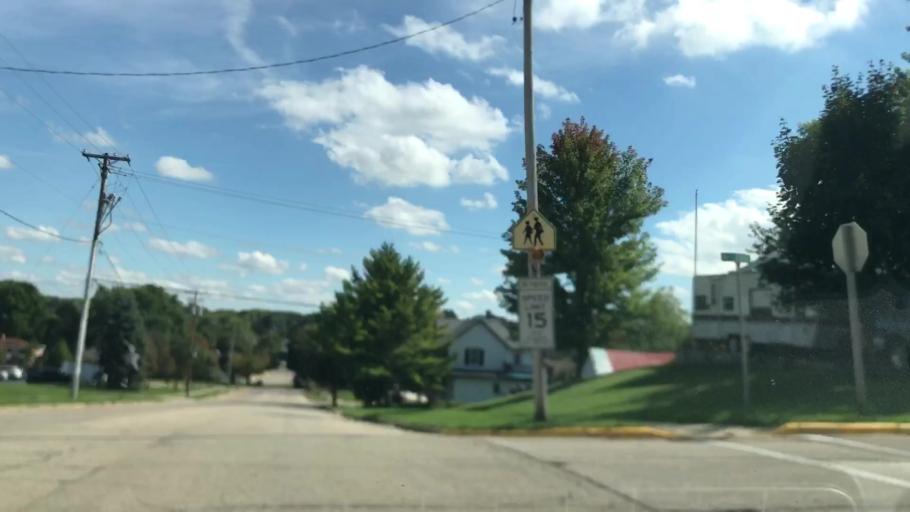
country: US
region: Wisconsin
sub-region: Dodge County
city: Mayville
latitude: 43.5012
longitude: -88.5550
